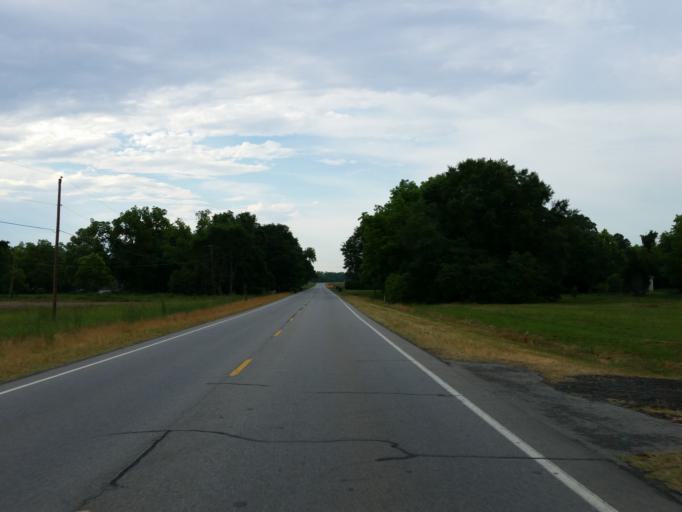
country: US
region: Georgia
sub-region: Dooly County
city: Vienna
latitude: 32.0382
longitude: -83.7938
